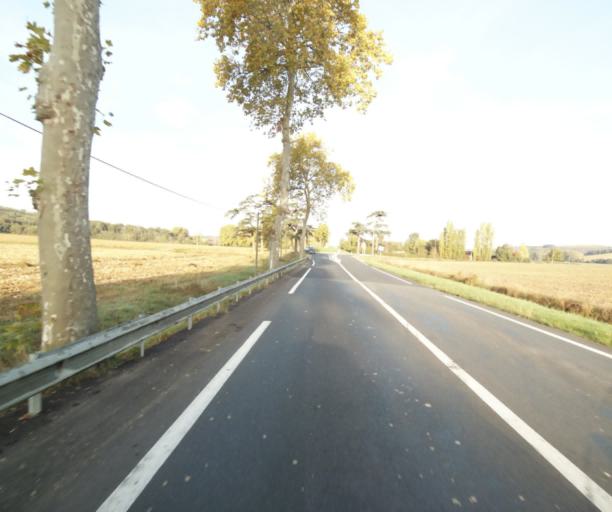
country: FR
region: Midi-Pyrenees
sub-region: Departement du Tarn-et-Garonne
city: Saint-Nauphary
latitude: 43.9436
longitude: 1.4649
